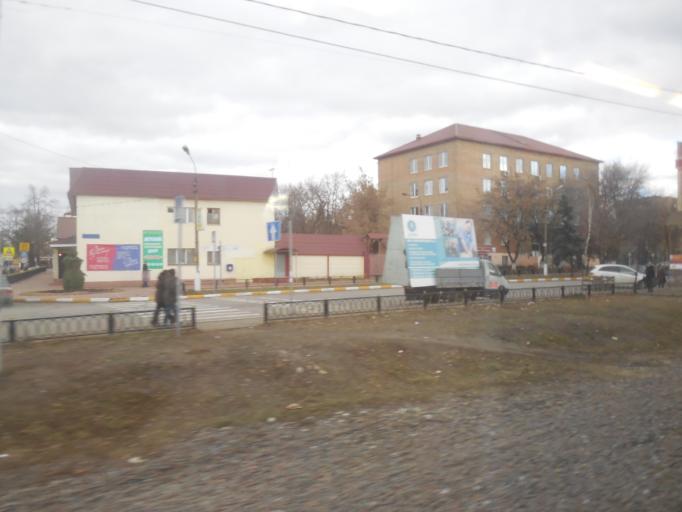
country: RU
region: Moskovskaya
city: Ramenskoye
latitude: 55.5669
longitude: 38.2221
